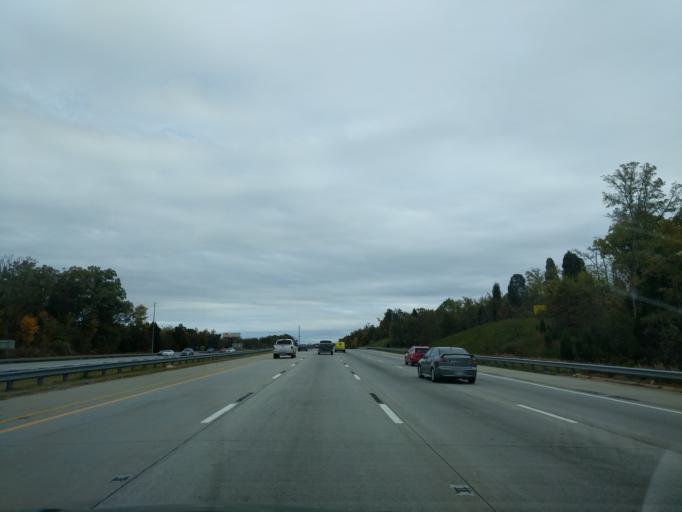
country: US
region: North Carolina
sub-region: Rowan County
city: East Spencer
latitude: 35.6685
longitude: -80.4366
